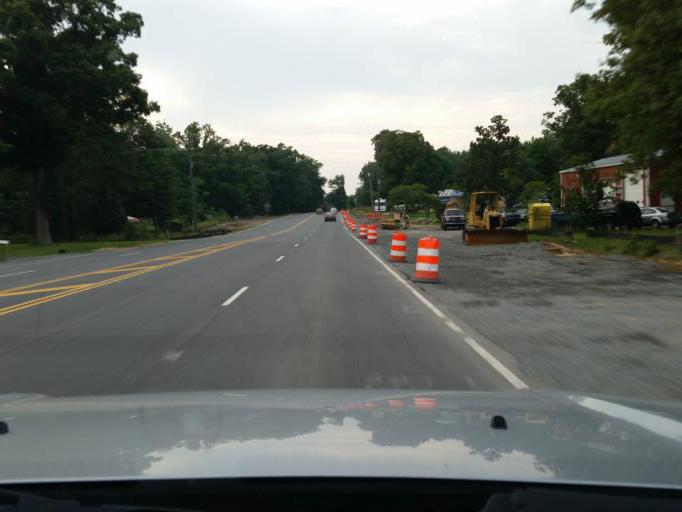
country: US
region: Virginia
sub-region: Spotsylvania County
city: Spotsylvania Courthouse
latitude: 38.1365
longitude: -77.5220
